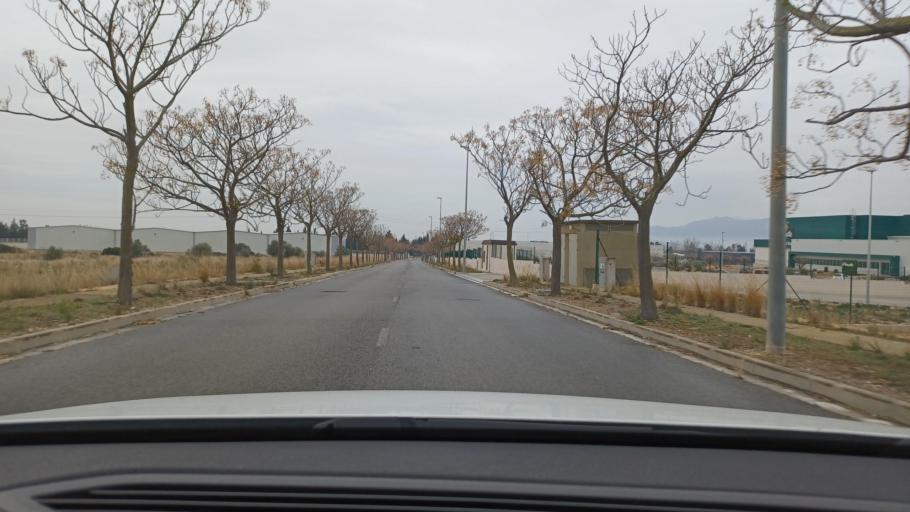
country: ES
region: Catalonia
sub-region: Provincia de Tarragona
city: Amposta
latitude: 40.7597
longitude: 0.6002
